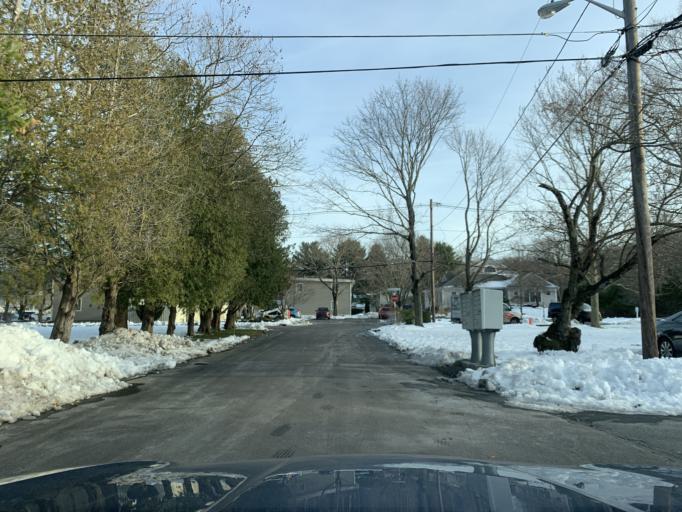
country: US
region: Rhode Island
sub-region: Washington County
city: North Kingstown
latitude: 41.5950
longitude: -71.4413
